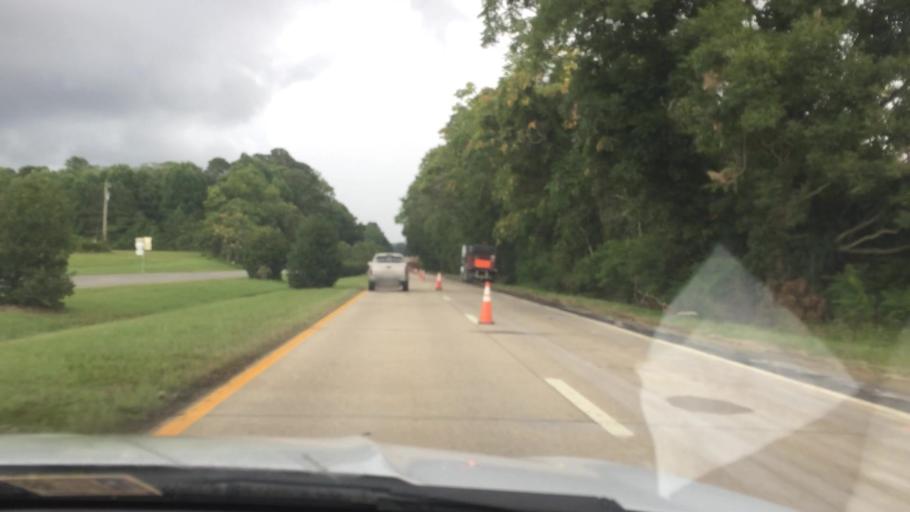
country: US
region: Virginia
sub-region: King William County
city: West Point
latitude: 37.4010
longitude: -76.8062
